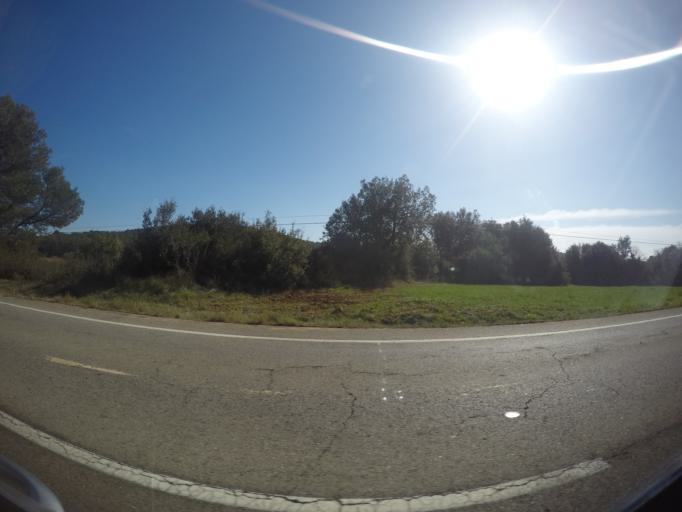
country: ES
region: Catalonia
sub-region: Provincia de Girona
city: Ventallo
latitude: 42.1404
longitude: 3.0145
